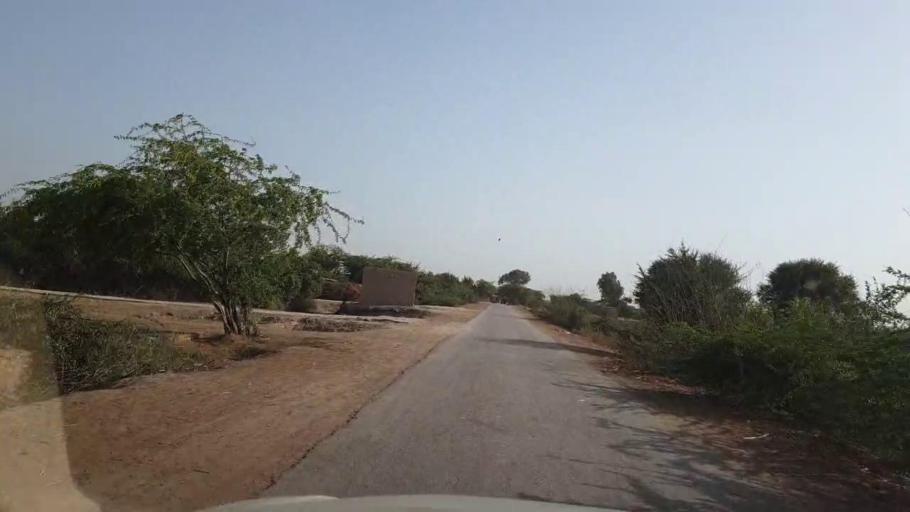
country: PK
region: Sindh
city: Tando Ghulam Ali
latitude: 25.0871
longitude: 68.8689
